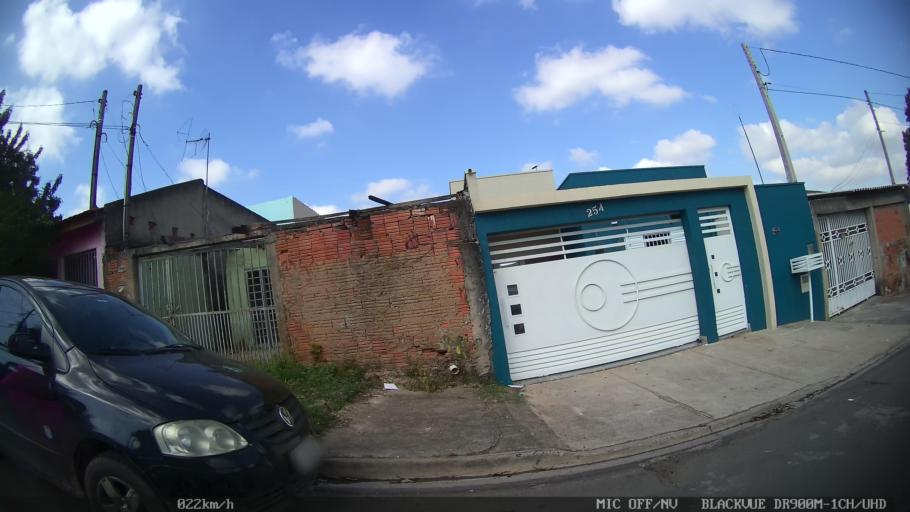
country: BR
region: Sao Paulo
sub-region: Indaiatuba
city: Indaiatuba
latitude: -22.9734
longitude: -47.1788
